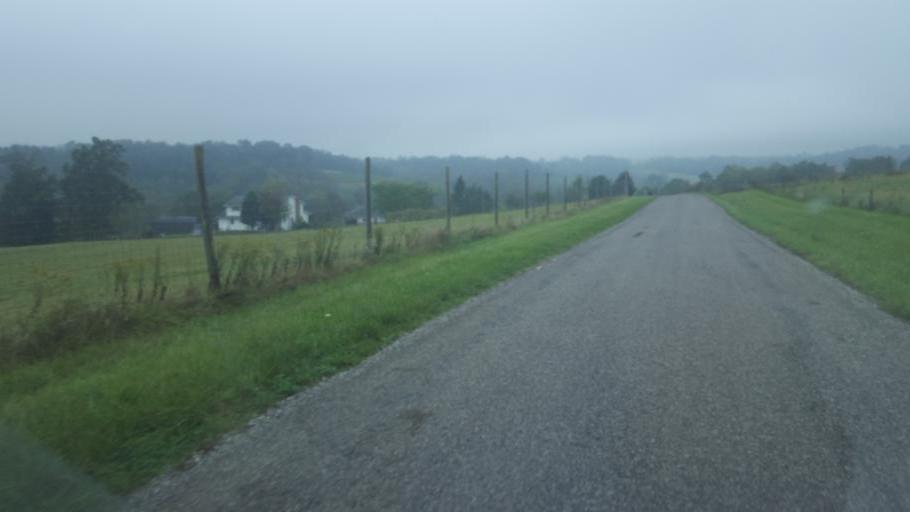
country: US
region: Ohio
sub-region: Tuscarawas County
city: Sugarcreek
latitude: 40.5774
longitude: -81.7521
